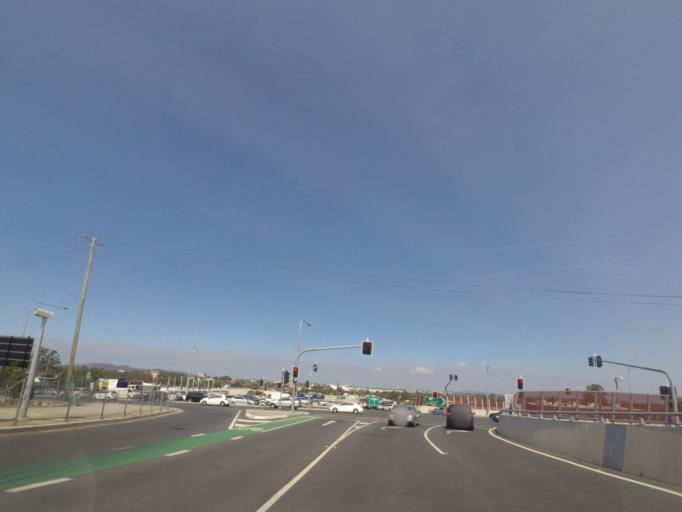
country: AU
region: Queensland
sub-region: Brisbane
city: Nathan
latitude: -27.5606
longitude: 153.0655
